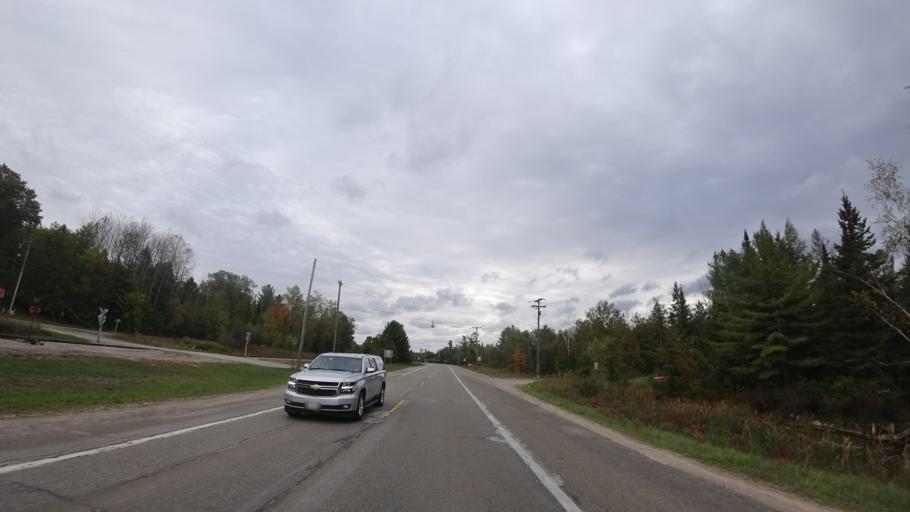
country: US
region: Michigan
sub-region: Charlevoix County
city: Boyne City
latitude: 45.1616
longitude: -84.9188
